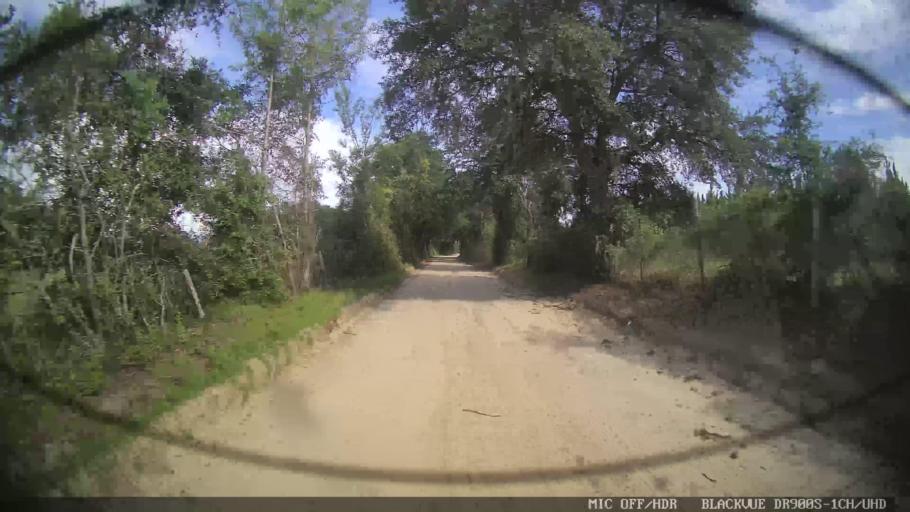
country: US
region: Georgia
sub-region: Echols County
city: Statenville
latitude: 30.6314
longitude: -83.1926
